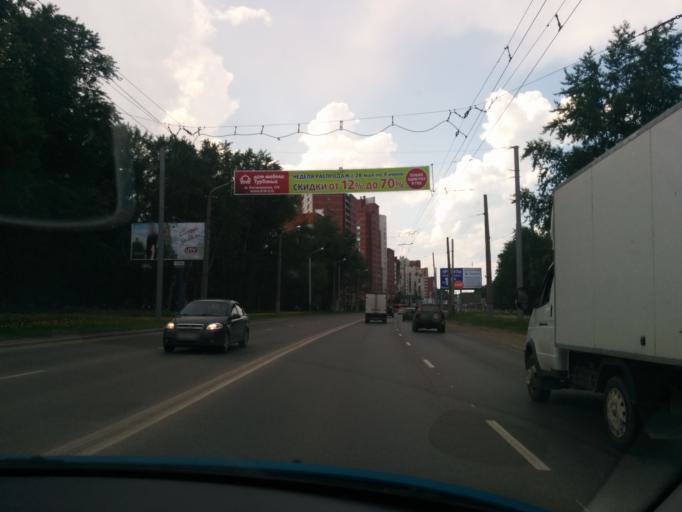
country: RU
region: Perm
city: Kondratovo
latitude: 57.9812
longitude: 56.1776
